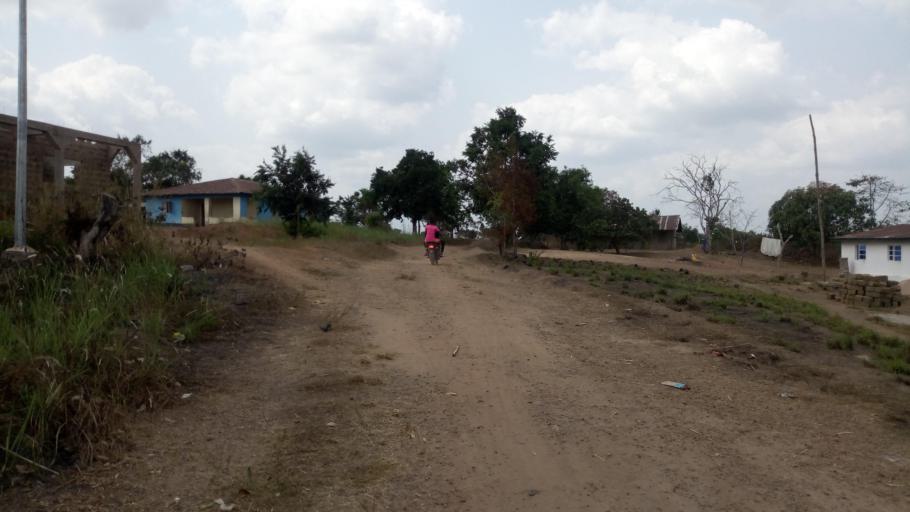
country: SL
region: Southern Province
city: Mogbwemo
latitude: 7.7936
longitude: -12.3031
